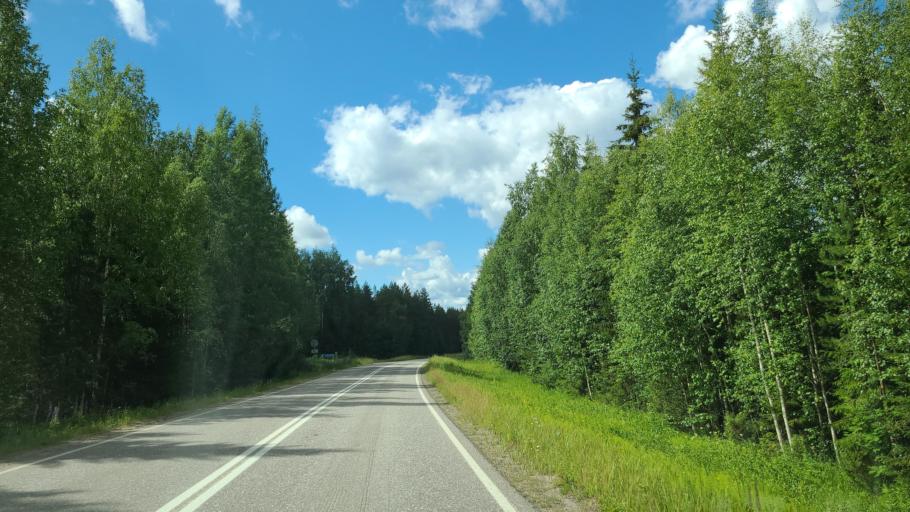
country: FI
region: North Karelia
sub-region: Joensuu
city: Outokumpu
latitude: 62.9896
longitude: 28.8266
